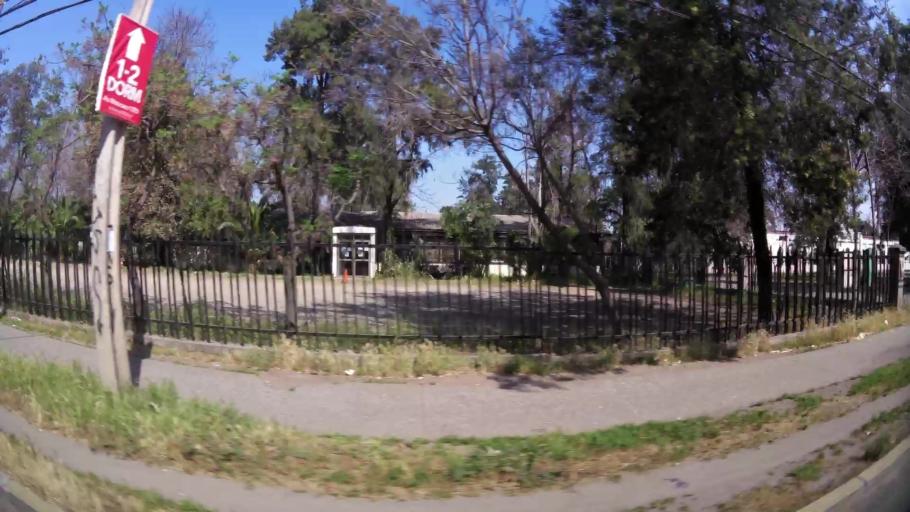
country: CL
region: Santiago Metropolitan
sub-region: Provincia de Santiago
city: Santiago
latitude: -33.4441
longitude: -70.6818
